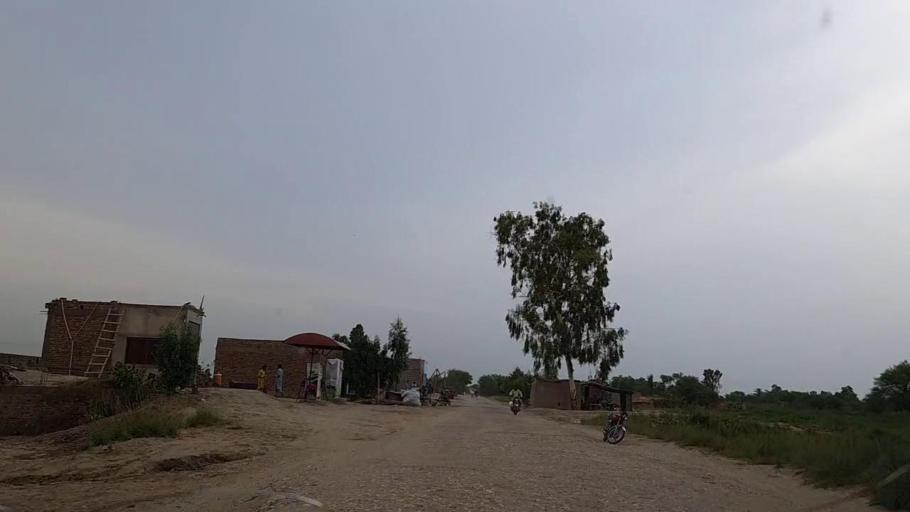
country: PK
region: Sindh
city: Mirpur Mathelo
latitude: 27.9016
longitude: 69.6586
